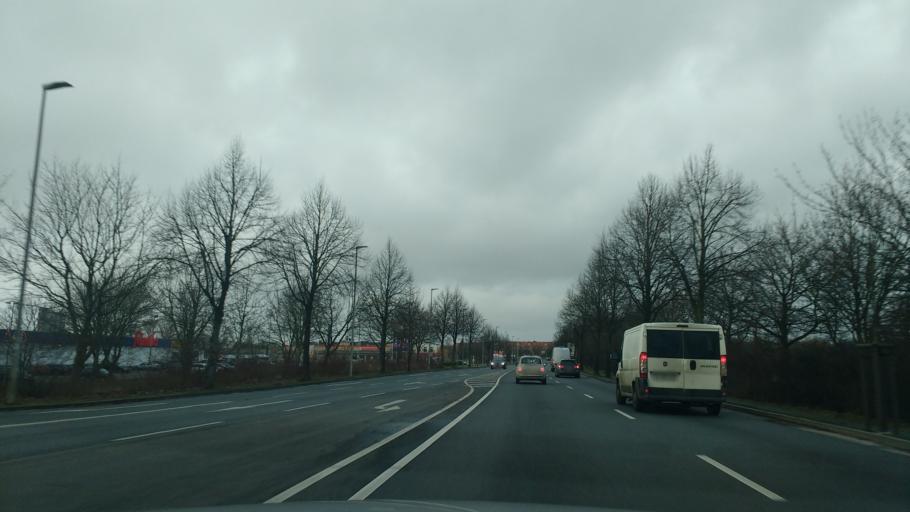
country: DE
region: Schleswig-Holstein
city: Itzehoe
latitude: 53.9134
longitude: 9.5161
